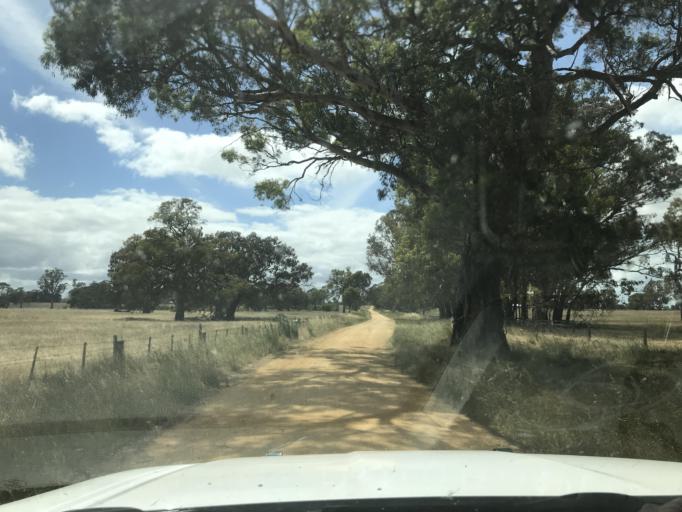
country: AU
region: South Australia
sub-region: Naracoorte and Lucindale
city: Naracoorte
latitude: -37.0193
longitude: 141.1008
